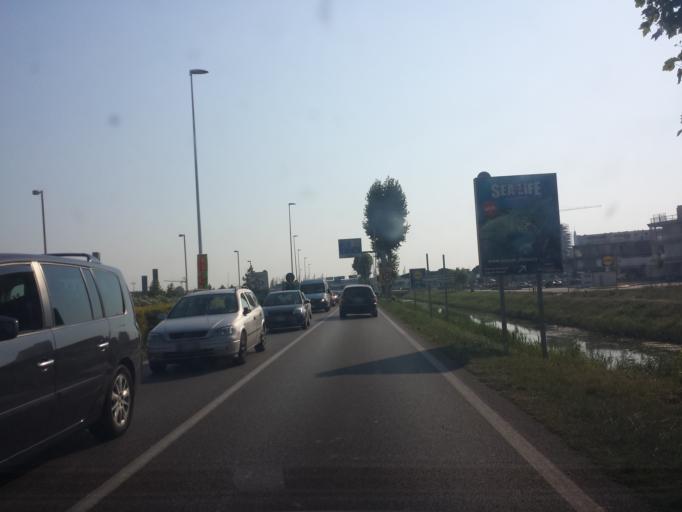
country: IT
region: Veneto
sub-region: Provincia di Venezia
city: Lido di Iesolo
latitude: 45.5064
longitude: 12.6304
